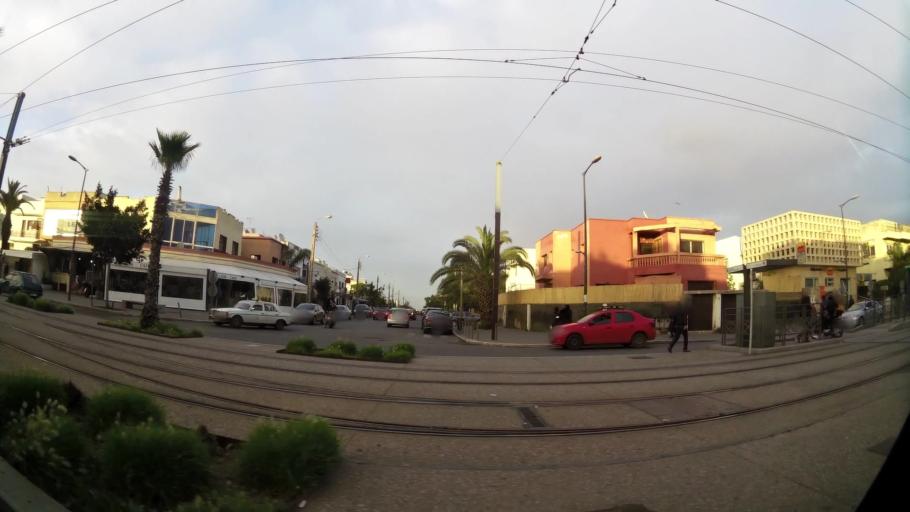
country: MA
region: Grand Casablanca
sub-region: Casablanca
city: Casablanca
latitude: 33.5725
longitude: -7.6697
